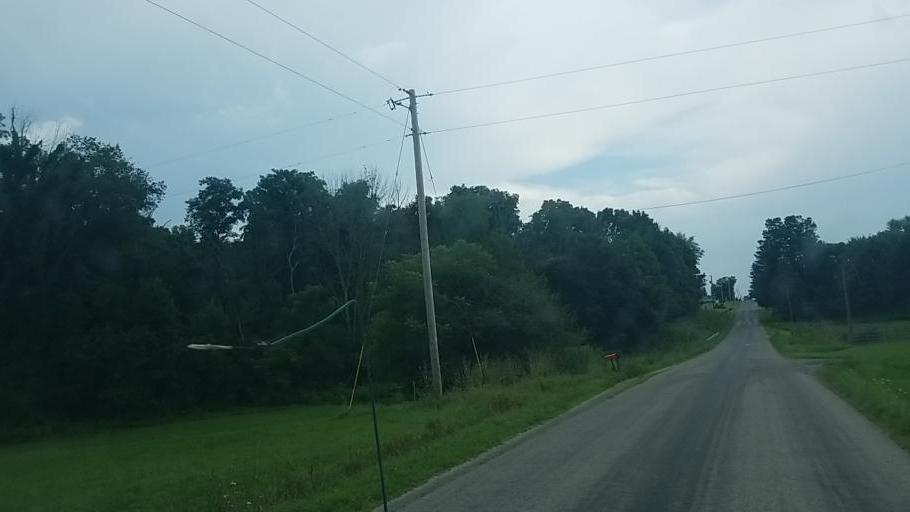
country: US
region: Ohio
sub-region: Wayne County
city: Creston
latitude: 40.9626
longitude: -81.9379
